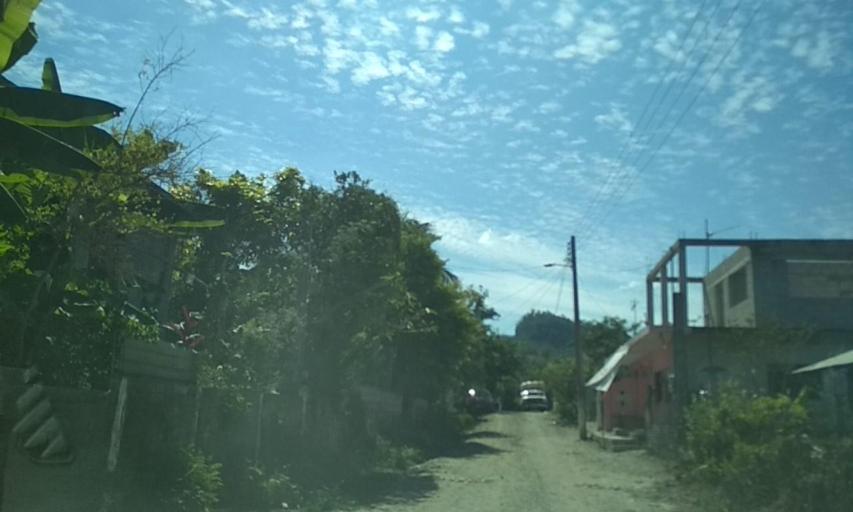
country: MX
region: Veracruz
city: Cazones de Herrera
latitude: 20.6422
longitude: -97.3066
